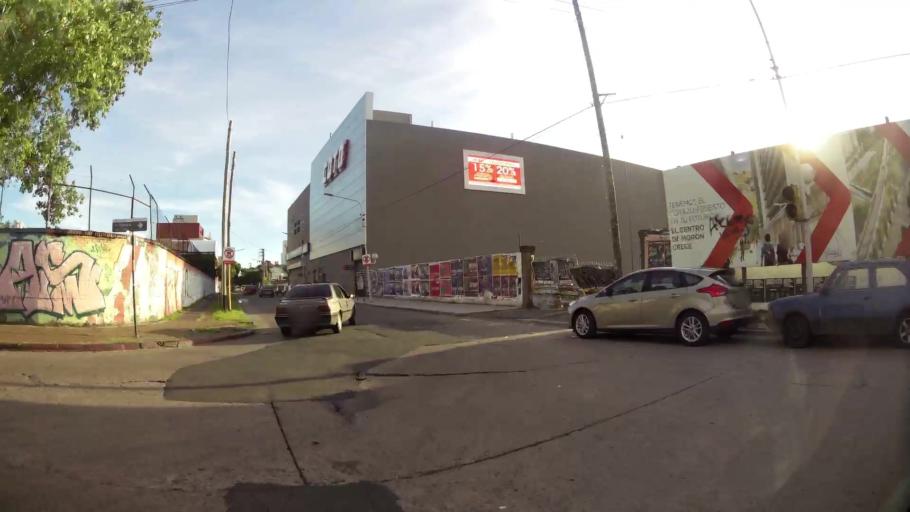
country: AR
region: Buenos Aires
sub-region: Partido de Moron
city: Moron
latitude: -34.6492
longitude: -58.6252
